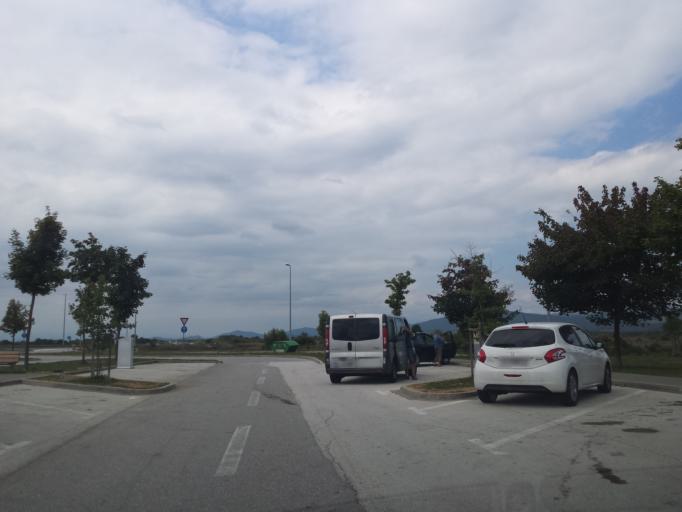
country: HR
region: Zadarska
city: Starigrad
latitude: 44.4631
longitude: 15.6024
